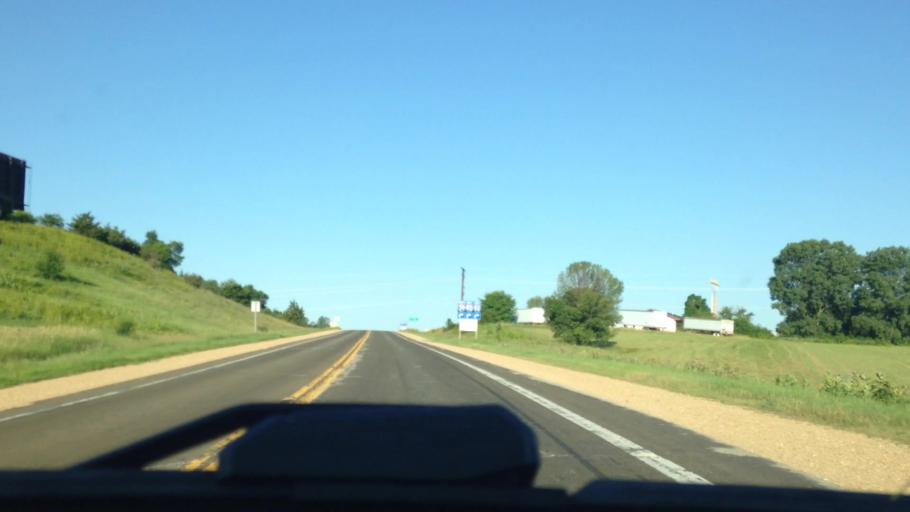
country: US
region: Wisconsin
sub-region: Columbia County
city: Poynette
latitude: 43.3374
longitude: -89.4480
